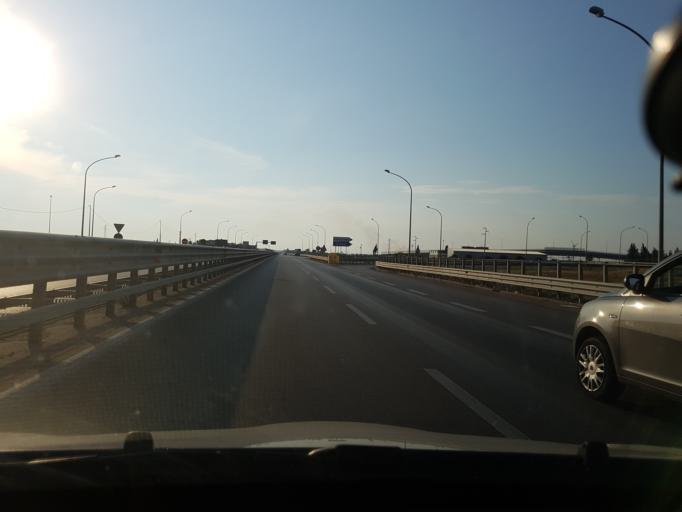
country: IT
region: Apulia
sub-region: Provincia di Foggia
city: Orta Nova
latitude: 41.3456
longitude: 15.7368
